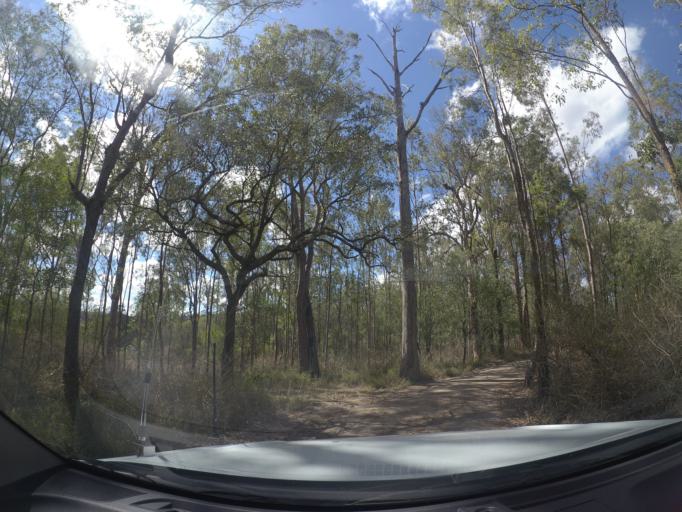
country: AU
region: Queensland
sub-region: Logan
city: Cedar Vale
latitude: -27.8379
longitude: 152.9744
